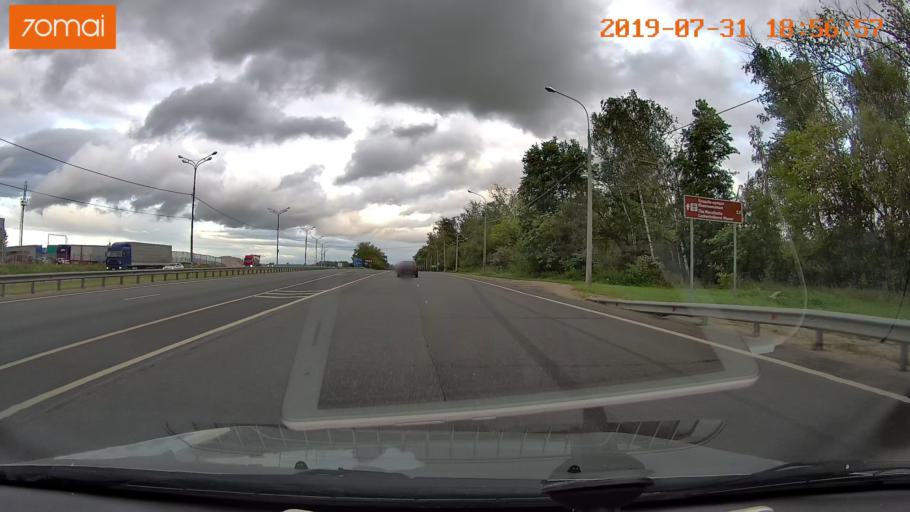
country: RU
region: Moskovskaya
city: Raduzhnyy
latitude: 55.1582
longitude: 38.6855
